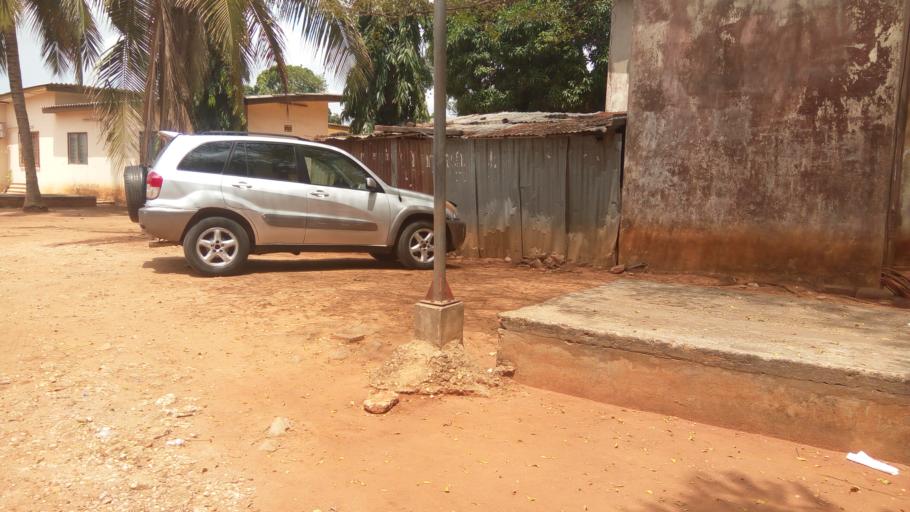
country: BJ
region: Atlantique
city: Abomey-Calavi
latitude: 6.4125
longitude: 2.3389
